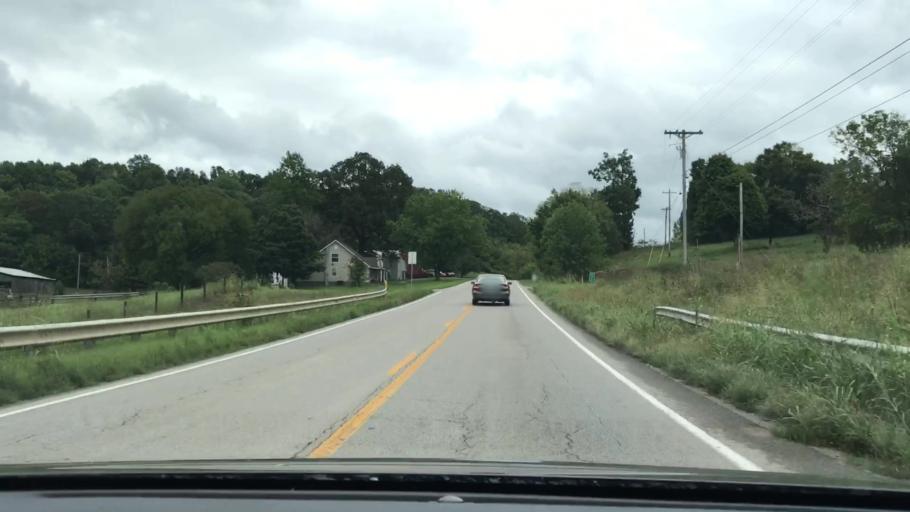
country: US
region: Kentucky
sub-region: Metcalfe County
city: Edmonton
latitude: 36.9060
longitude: -85.7575
